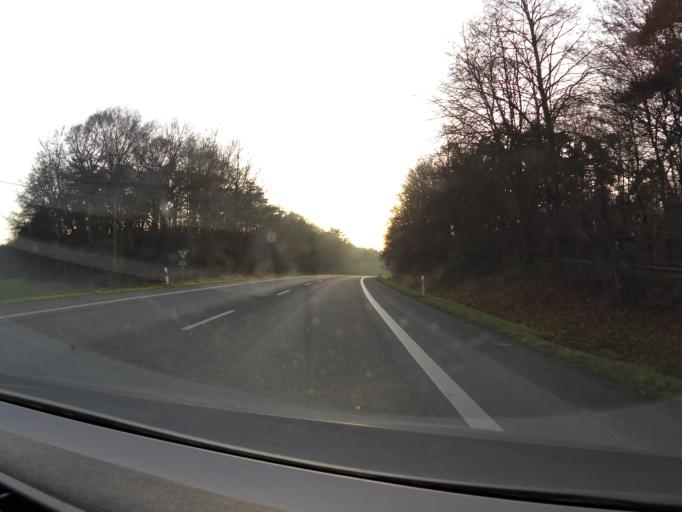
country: DE
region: North Rhine-Westphalia
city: Straelen
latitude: 51.3837
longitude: 6.2650
